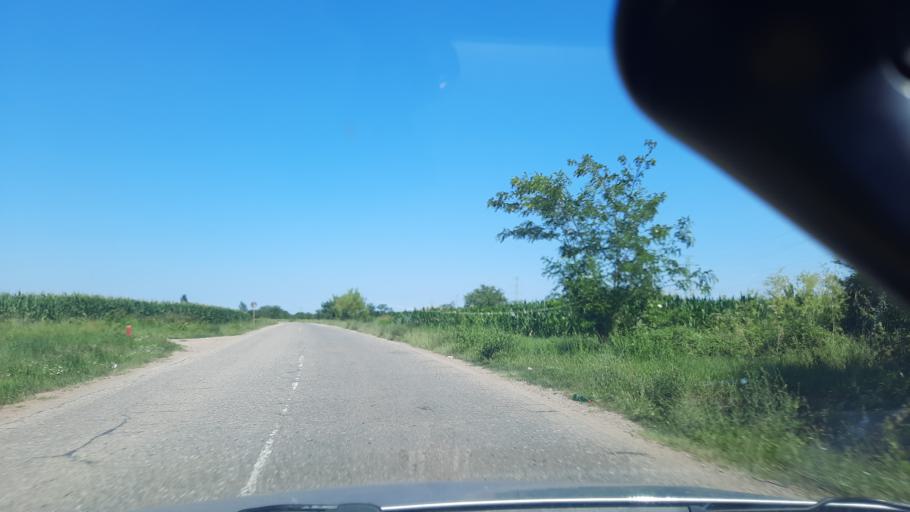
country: RS
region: Central Serbia
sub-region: Podunavski Okrug
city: Smederevo
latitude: 44.5887
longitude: 20.9751
